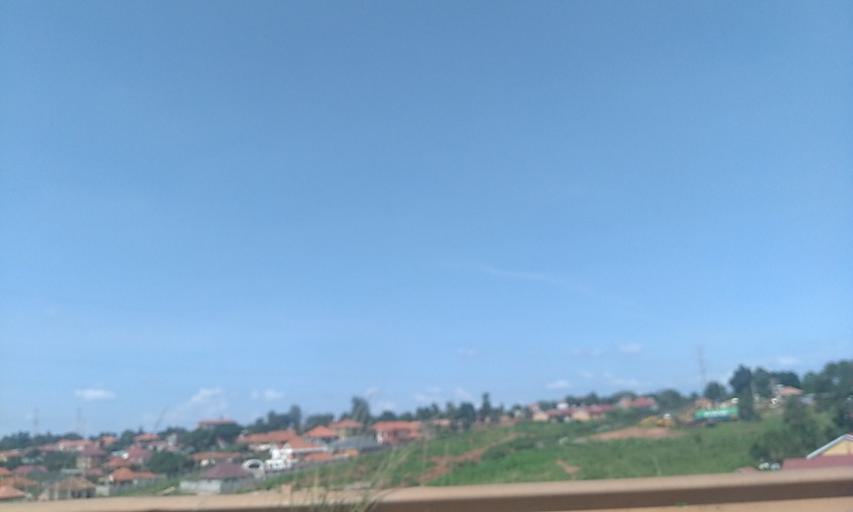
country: UG
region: Central Region
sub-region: Wakiso District
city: Kireka
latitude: 0.3664
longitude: 32.6456
